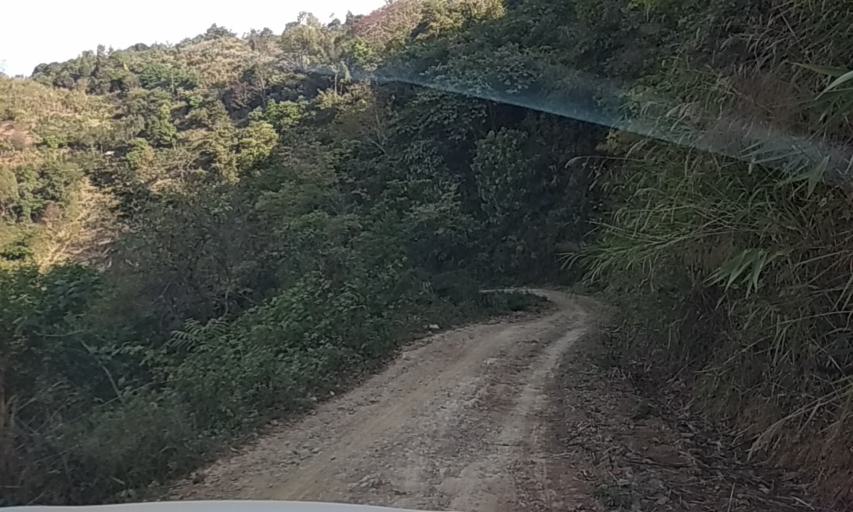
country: LA
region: Phongsali
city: Phongsali
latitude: 21.6895
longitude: 102.1013
